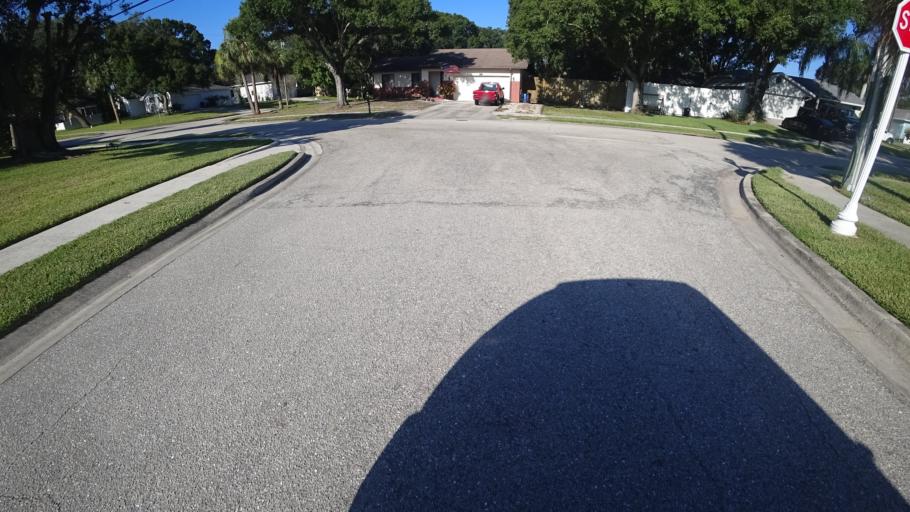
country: US
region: Florida
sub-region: Manatee County
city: Ellenton
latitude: 27.5023
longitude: -82.5092
